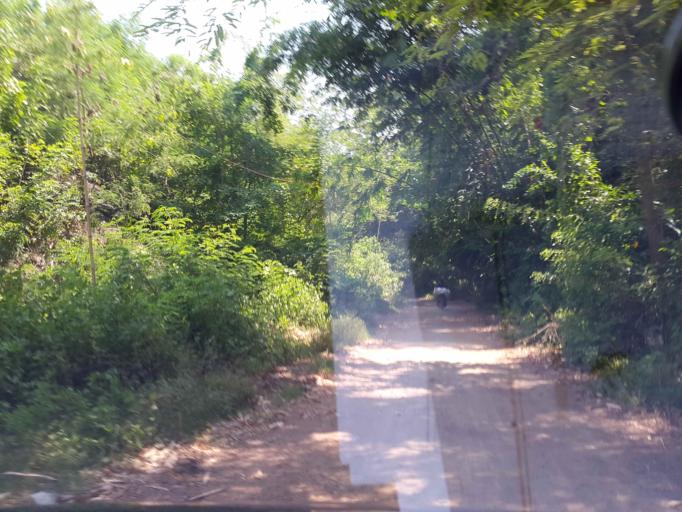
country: ID
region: West Nusa Tenggara
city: Karangkebon Timur
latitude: -8.6808
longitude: 116.0905
